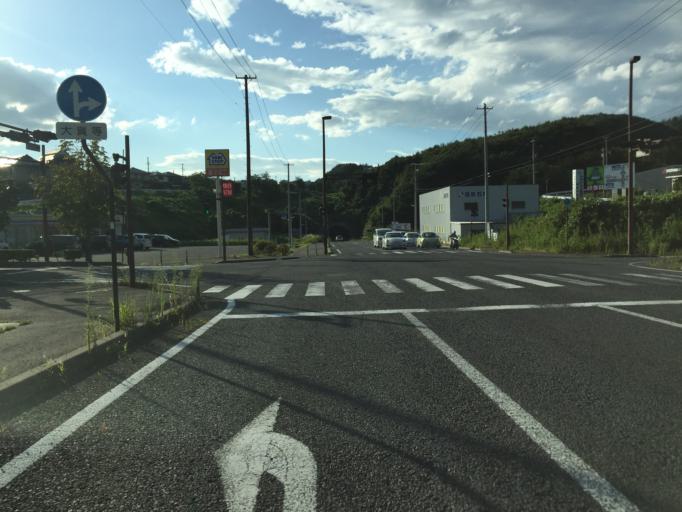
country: JP
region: Fukushima
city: Fukushima-shi
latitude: 37.7248
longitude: 140.4874
